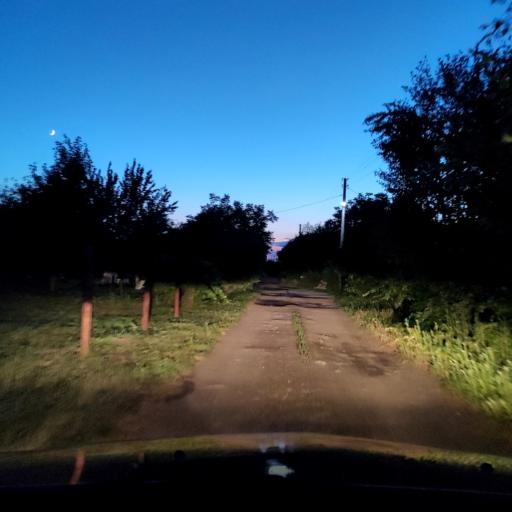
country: RU
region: Voronezj
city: Podgornoye
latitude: 51.8023
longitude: 39.2250
